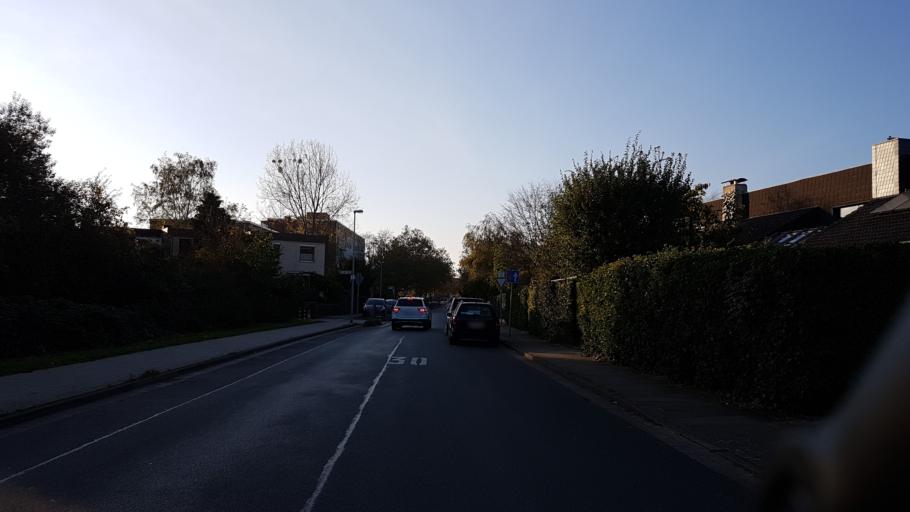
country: DE
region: Lower Saxony
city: Hemmingen
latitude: 52.3266
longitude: 9.7011
